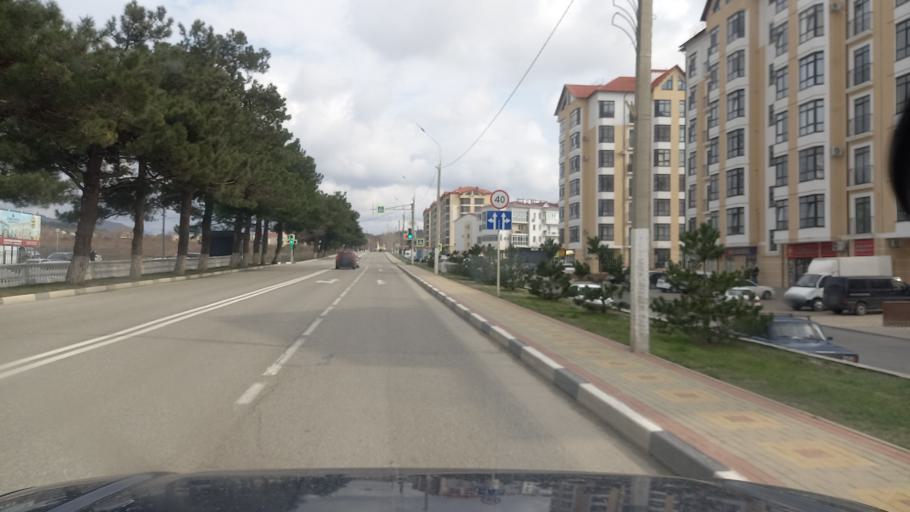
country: RU
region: Krasnodarskiy
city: Gelendzhik
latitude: 44.5565
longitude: 38.1051
